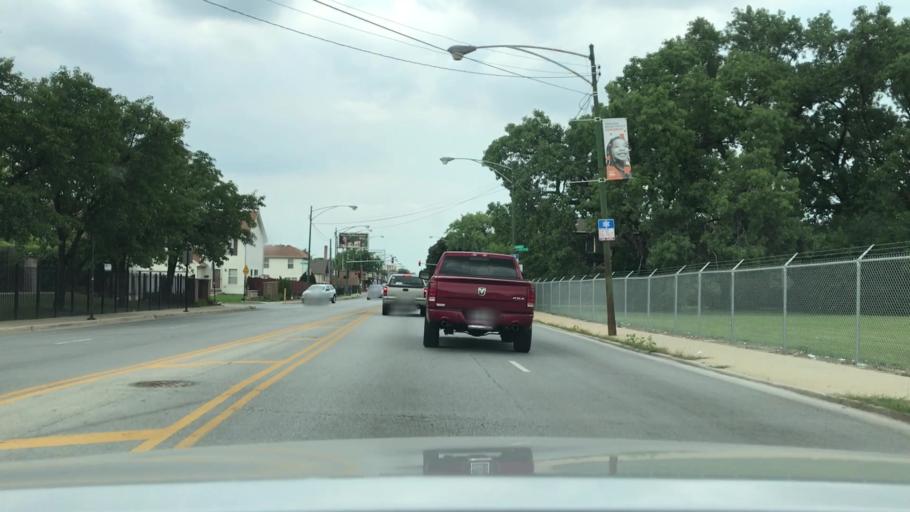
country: US
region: Illinois
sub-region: Cook County
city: Evergreen Park
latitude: 41.7375
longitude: -87.7020
